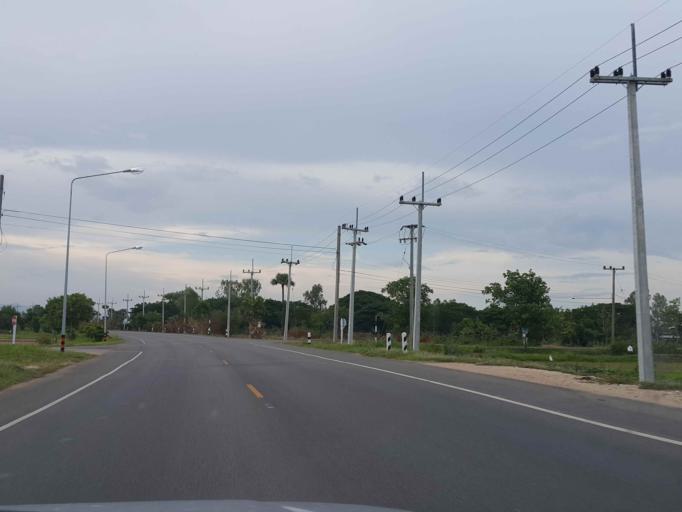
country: TH
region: Lampang
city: Ko Kha
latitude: 18.2220
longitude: 99.3965
